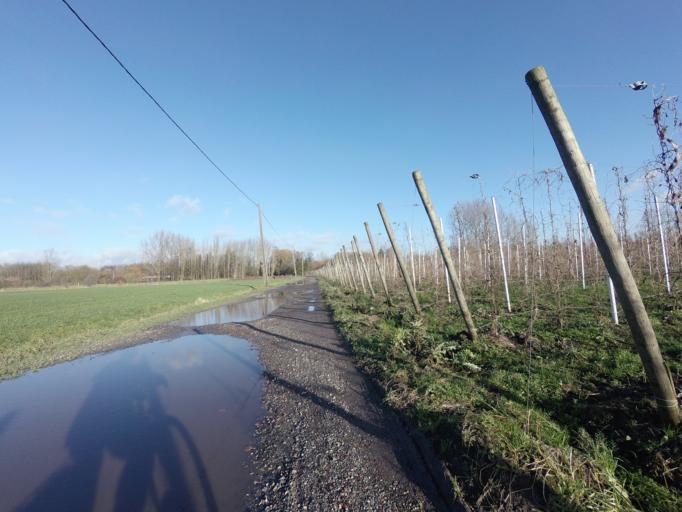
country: BE
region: Flanders
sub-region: Provincie Antwerpen
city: Lint
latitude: 51.1341
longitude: 4.5328
